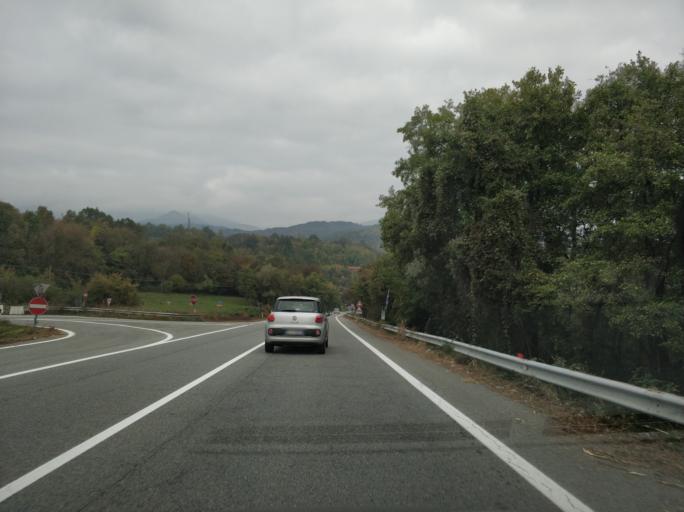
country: IT
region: Piedmont
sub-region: Provincia di Torino
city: Baldissero Canavese
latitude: 45.4093
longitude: 7.7543
